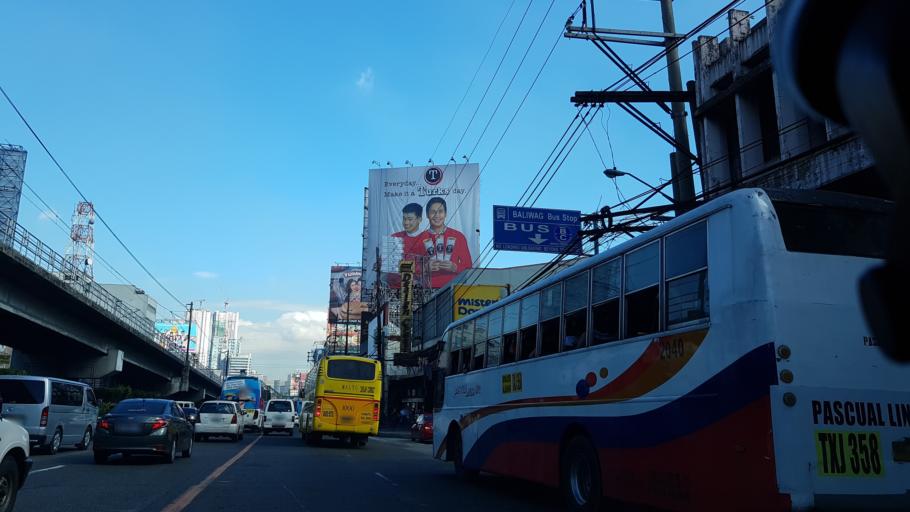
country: PH
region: Metro Manila
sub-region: Quezon City
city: Quezon City
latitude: 14.6242
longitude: 121.0491
